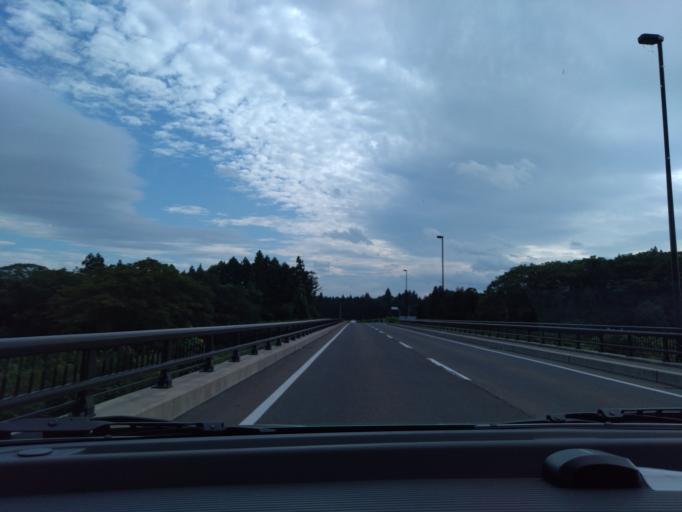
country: JP
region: Iwate
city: Hanamaki
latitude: 39.3790
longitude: 141.0568
